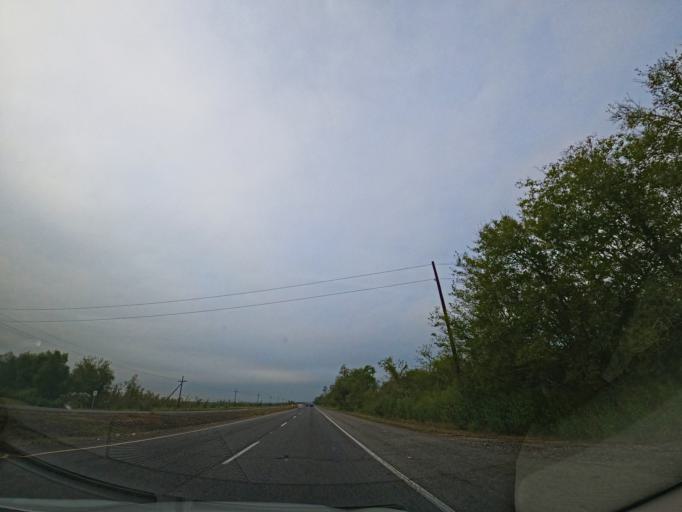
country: US
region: Louisiana
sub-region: Lafourche Parish
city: Raceland
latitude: 29.6836
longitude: -90.6468
